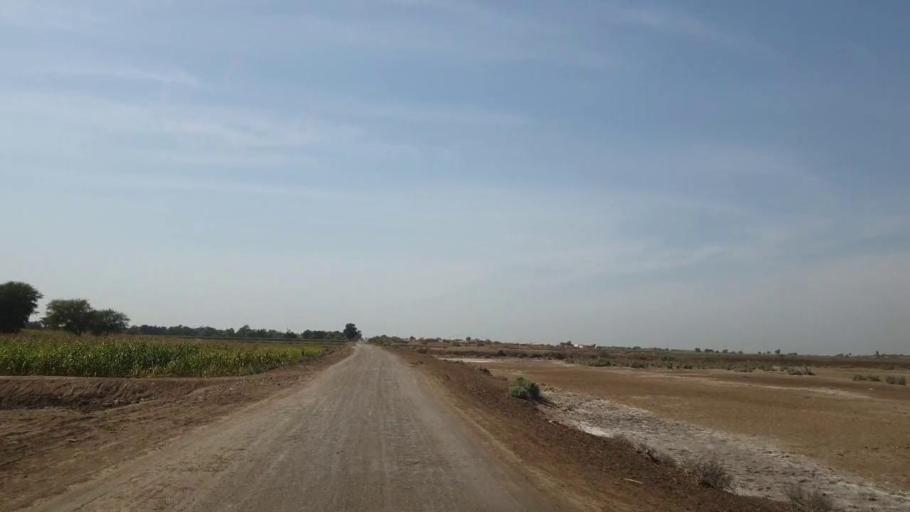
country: PK
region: Sindh
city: Kunri
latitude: 25.2182
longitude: 69.5312
